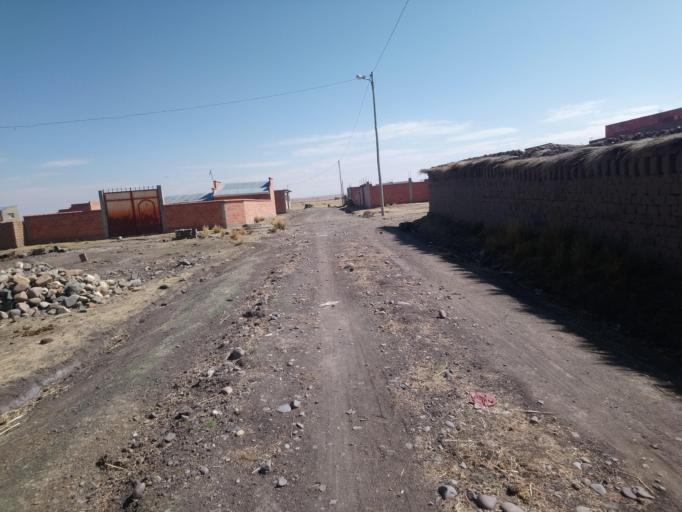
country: BO
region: La Paz
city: Batallas
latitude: -16.4376
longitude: -68.3742
